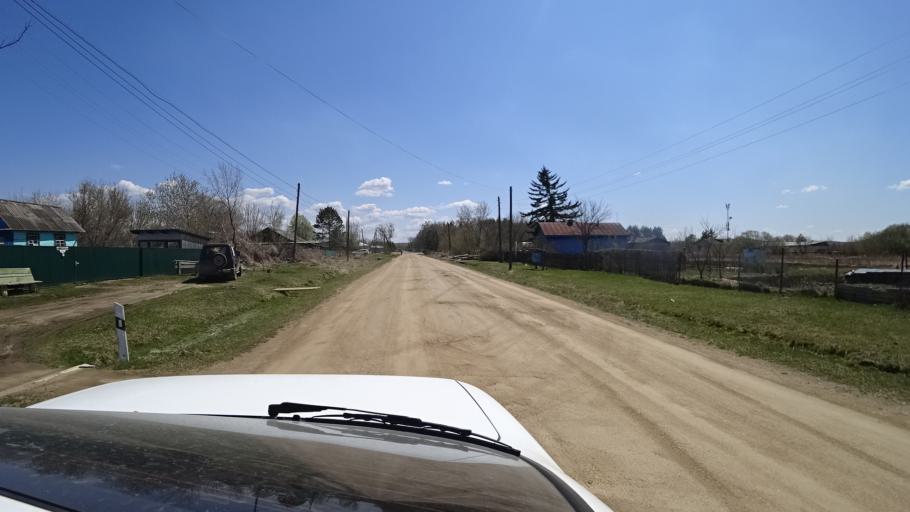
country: RU
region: Primorskiy
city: Dal'nerechensk
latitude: 45.7982
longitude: 133.7669
